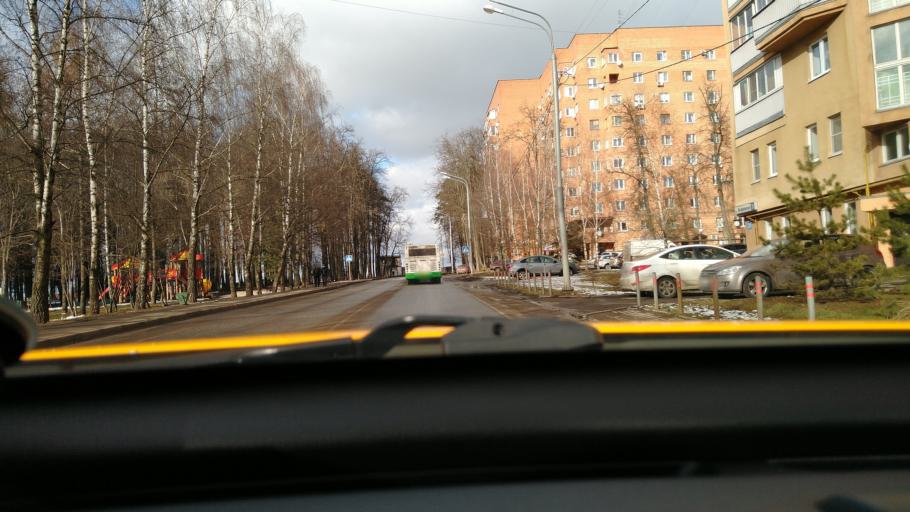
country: RU
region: Moskovskaya
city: Kommunarka
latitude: 55.5305
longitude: 37.4457
